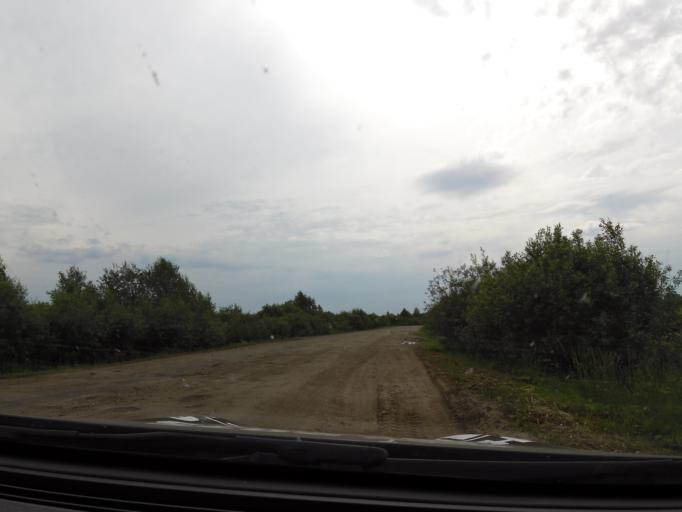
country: RU
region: Kostroma
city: Parfen'yevo
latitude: 58.3418
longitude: 43.4140
